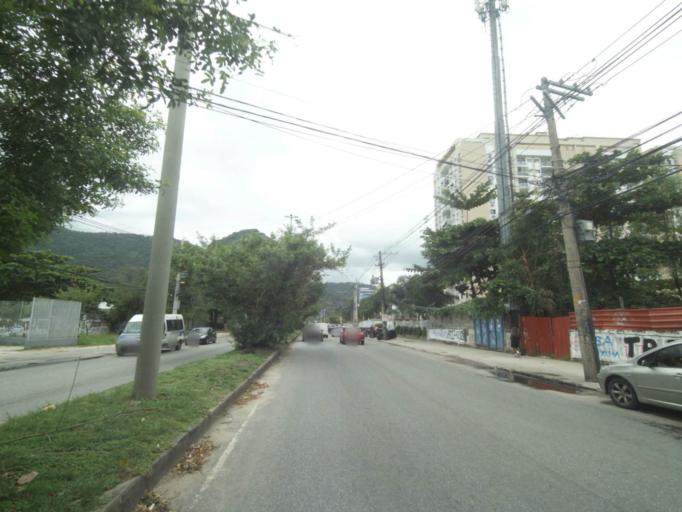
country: BR
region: Rio de Janeiro
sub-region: Nilopolis
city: Nilopolis
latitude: -22.9717
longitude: -43.4139
